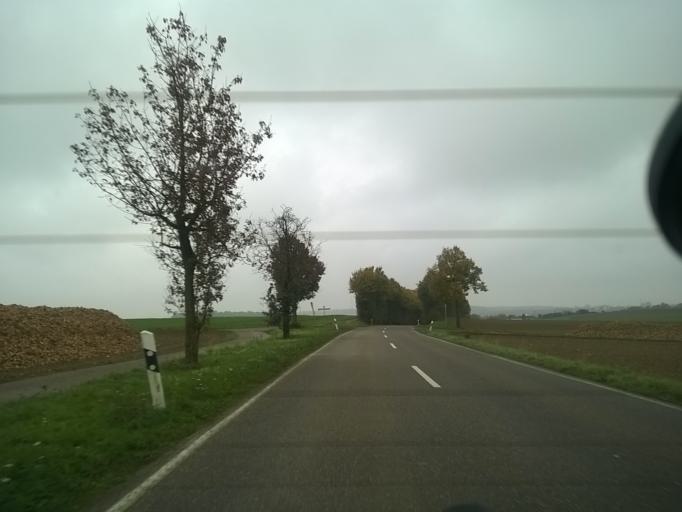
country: DE
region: Baden-Wuerttemberg
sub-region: Regierungsbezirk Stuttgart
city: Bad Wimpfen
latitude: 49.2076
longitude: 9.1487
